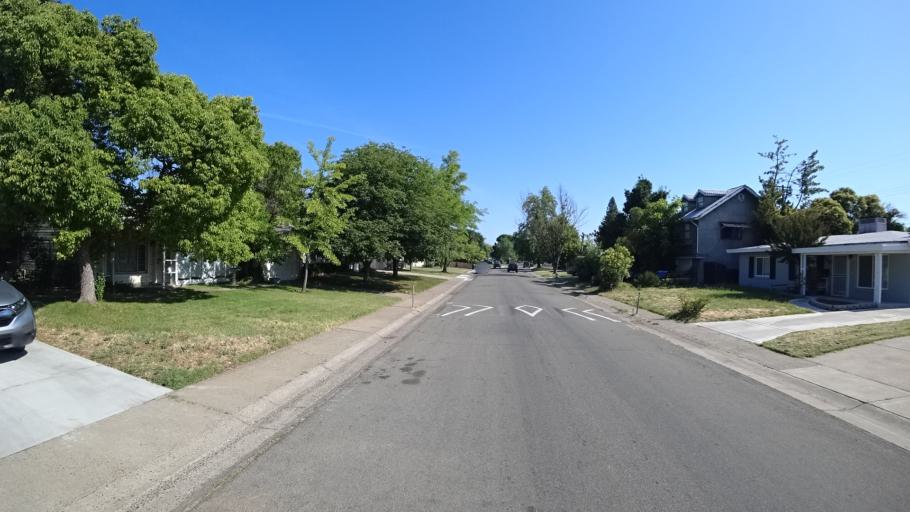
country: US
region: California
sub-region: Sacramento County
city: Florin
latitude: 38.5301
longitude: -121.4330
